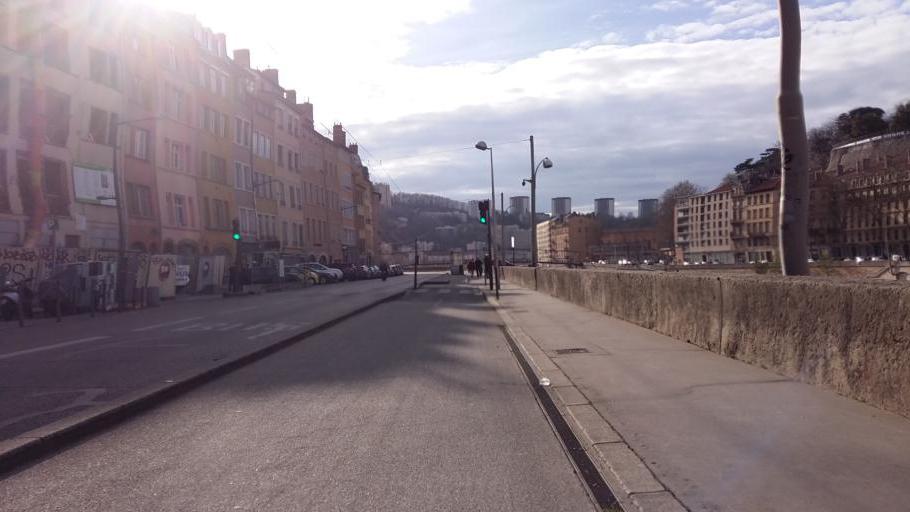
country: FR
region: Rhone-Alpes
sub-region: Departement du Rhone
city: Caluire-et-Cuire
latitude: 45.7674
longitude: 4.8243
